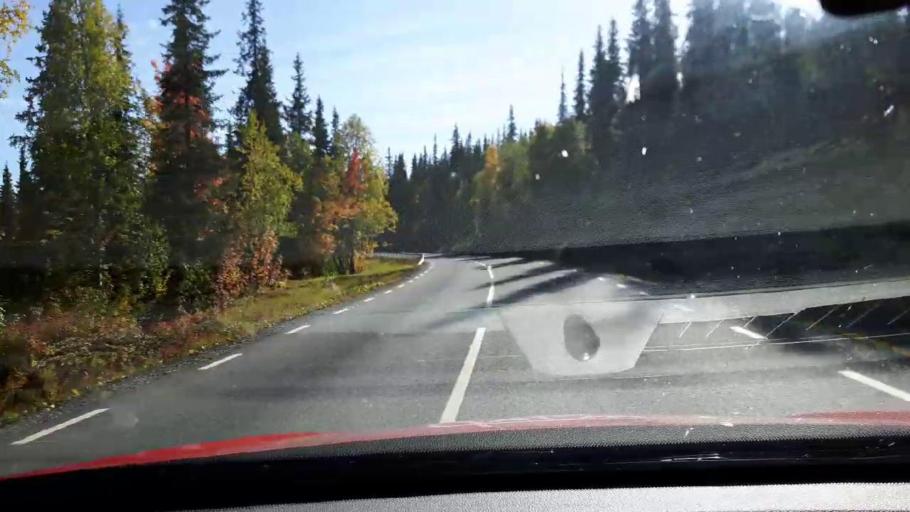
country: NO
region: Nord-Trondelag
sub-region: Royrvik
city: Royrvik
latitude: 64.8585
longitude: 14.1798
